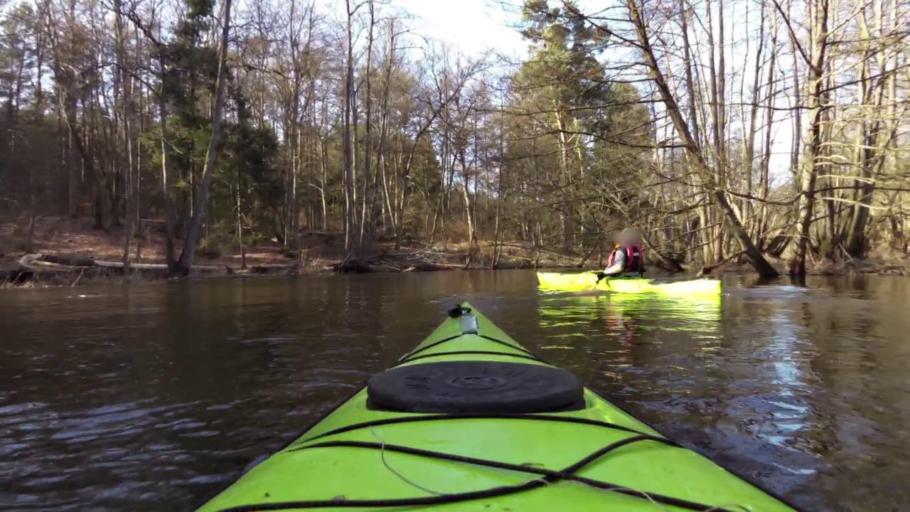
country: PL
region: West Pomeranian Voivodeship
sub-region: Powiat lobeski
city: Lobez
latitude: 53.7075
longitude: 15.5485
